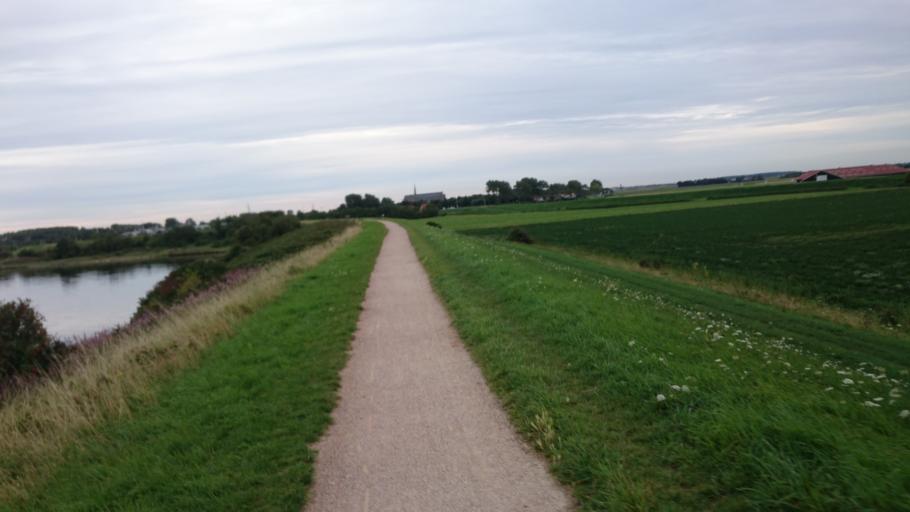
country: NL
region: Zeeland
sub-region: Schouwen-Duiveland
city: Scharendijke
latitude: 51.7347
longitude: 3.9050
